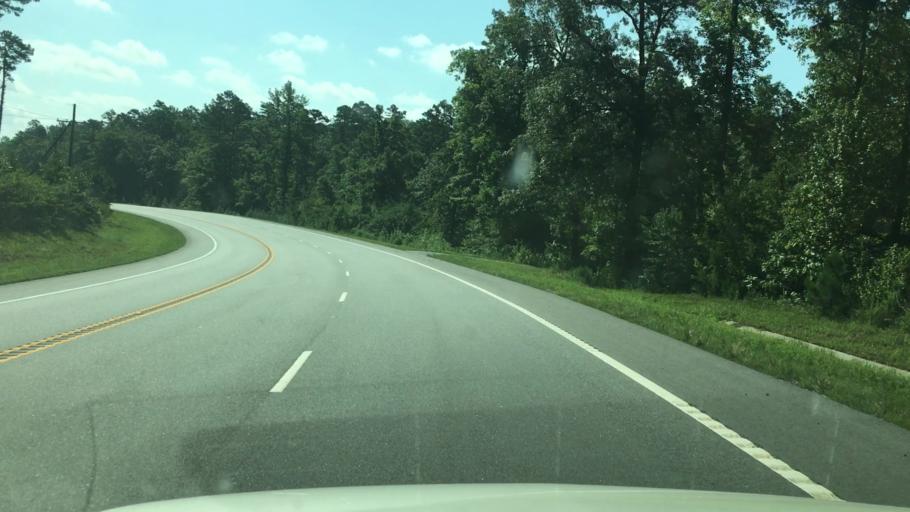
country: US
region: Arkansas
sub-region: Garland County
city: Rockwell
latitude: 34.5189
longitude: -93.3142
